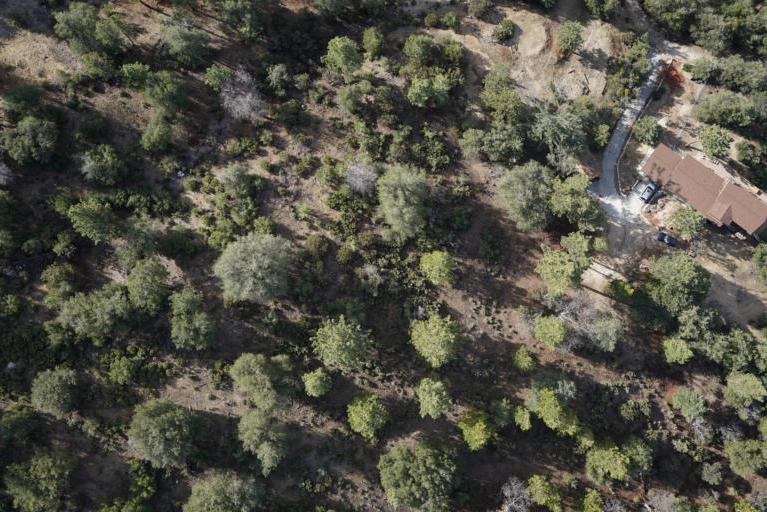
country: US
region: California
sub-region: Riverside County
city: Idyllwild
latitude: 33.7283
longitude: -116.7128
